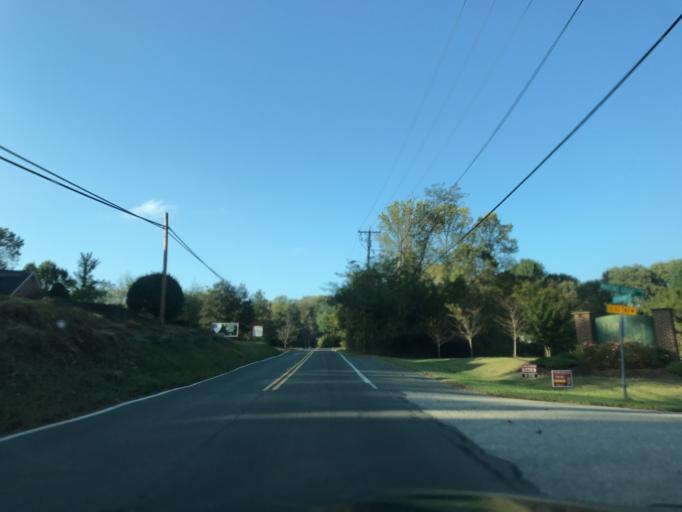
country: US
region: Maryland
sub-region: Anne Arundel County
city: Gambrills
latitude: 39.0291
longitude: -76.6506
